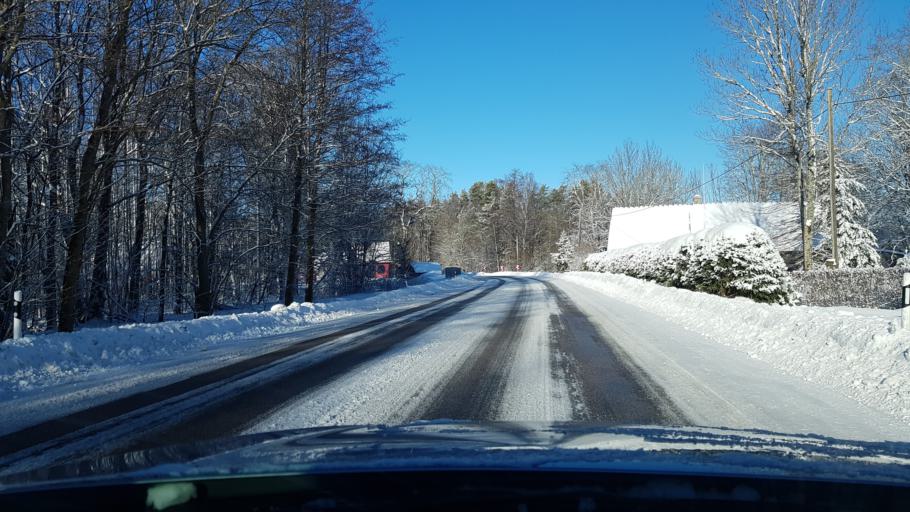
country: EE
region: Hiiumaa
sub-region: Kaerdla linn
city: Kardla
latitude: 58.9209
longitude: 22.7943
